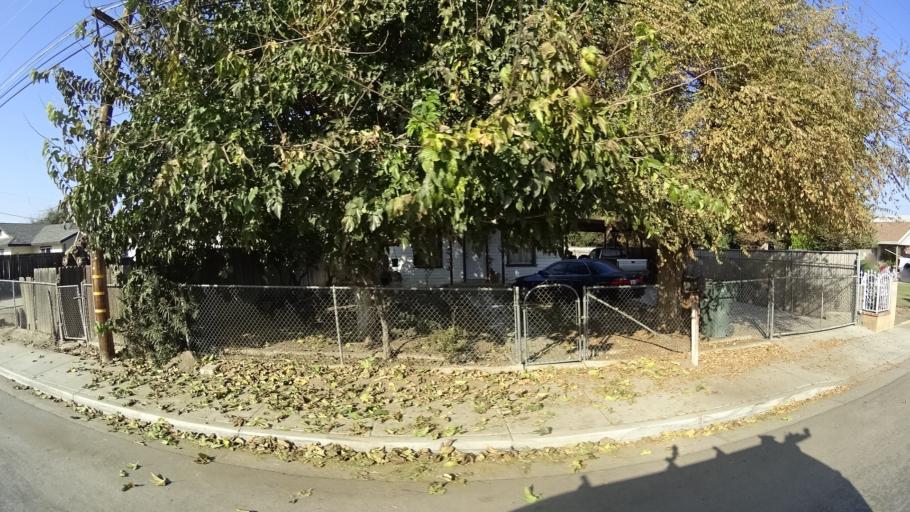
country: US
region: California
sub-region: Kern County
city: Greenfield
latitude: 35.2741
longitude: -119.0046
